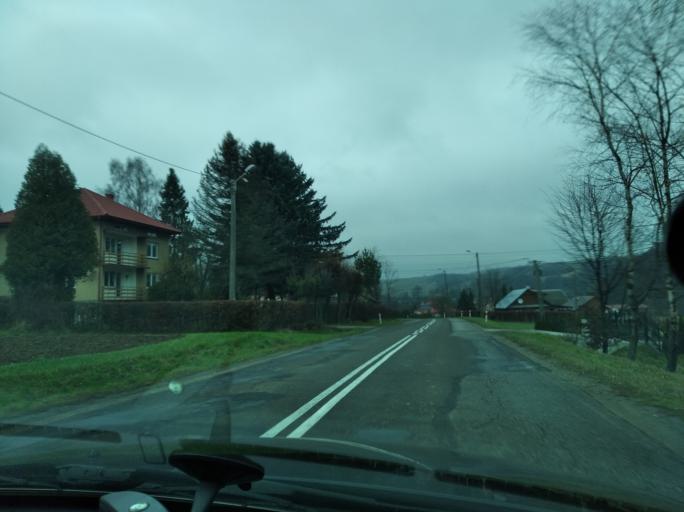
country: PL
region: Subcarpathian Voivodeship
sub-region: Powiat przeworski
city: Jawornik Polski
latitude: 49.8635
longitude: 22.2473
